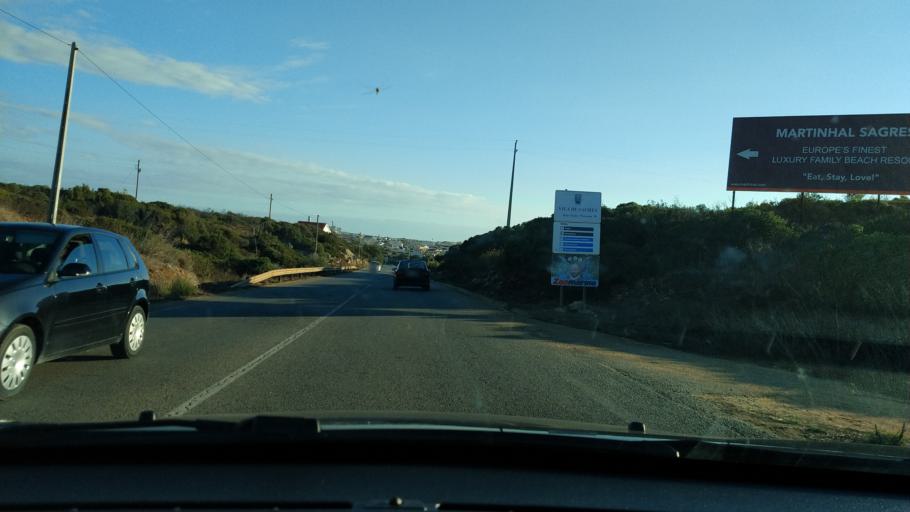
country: PT
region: Faro
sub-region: Vila do Bispo
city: Sagres
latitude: 37.0243
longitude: -8.9378
